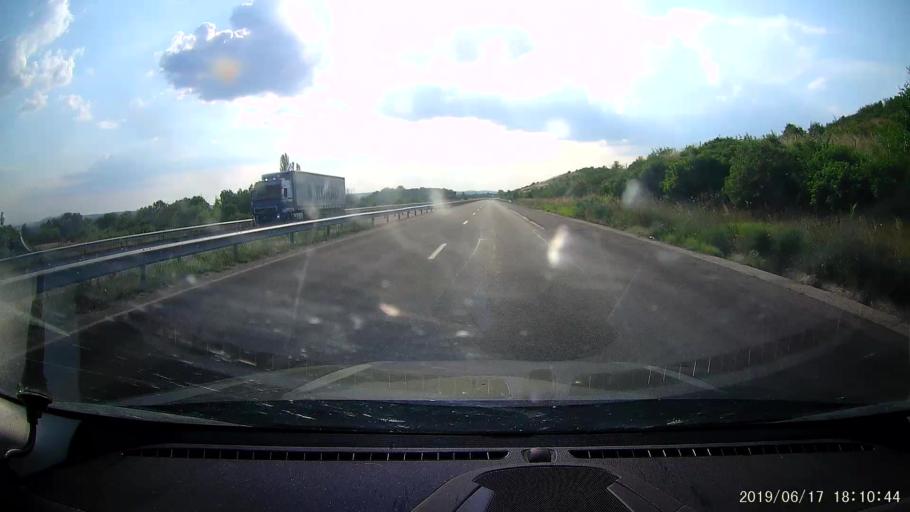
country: BG
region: Khaskovo
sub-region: Obshtina Lyubimets
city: Lyubimets
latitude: 41.8767
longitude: 26.0696
